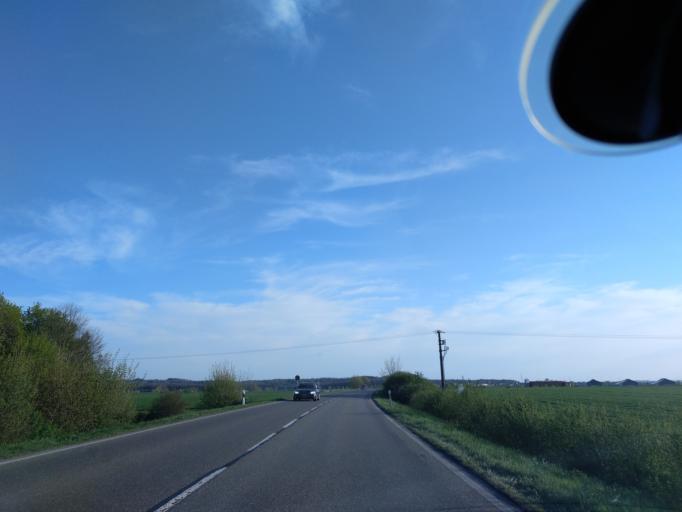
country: DE
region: Baden-Wuerttemberg
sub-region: Regierungsbezirk Stuttgart
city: Kirchberg an der Jagst
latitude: 49.1711
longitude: 9.9591
